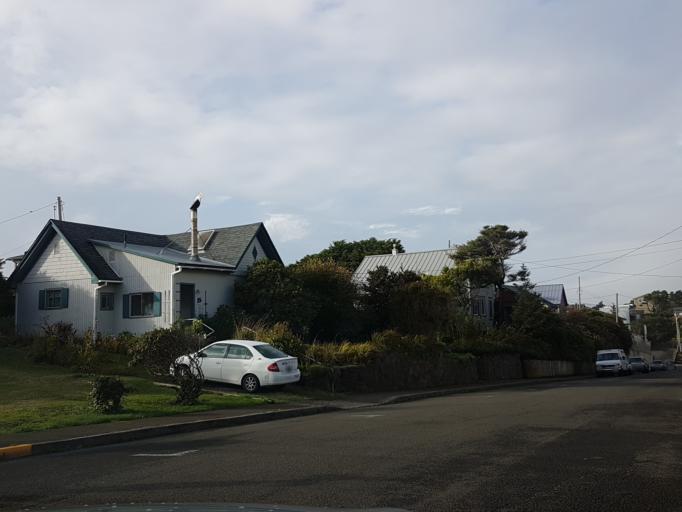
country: US
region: Oregon
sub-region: Lincoln County
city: Newport
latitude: 44.6366
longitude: -124.0590
